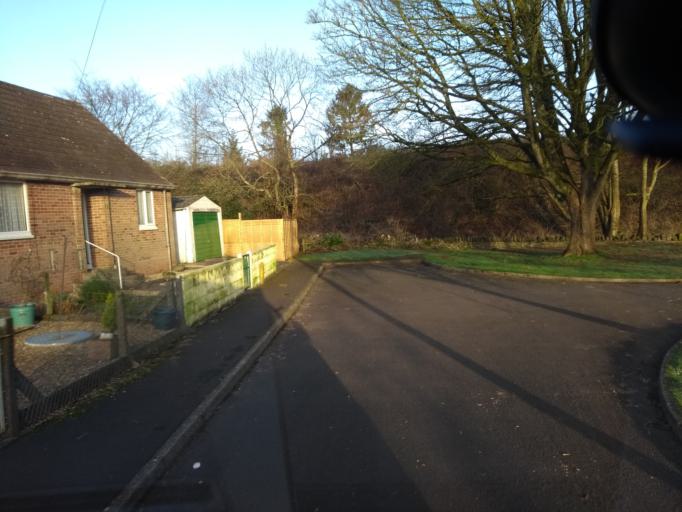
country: GB
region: England
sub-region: Somerset
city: Shepton Mallet
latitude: 51.1860
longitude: -2.5562
